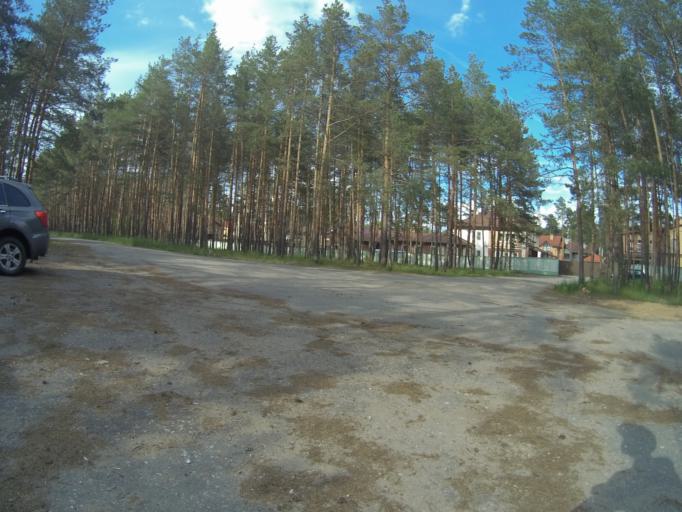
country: RU
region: Vladimir
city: Kommunar
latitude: 56.0853
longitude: 40.4382
